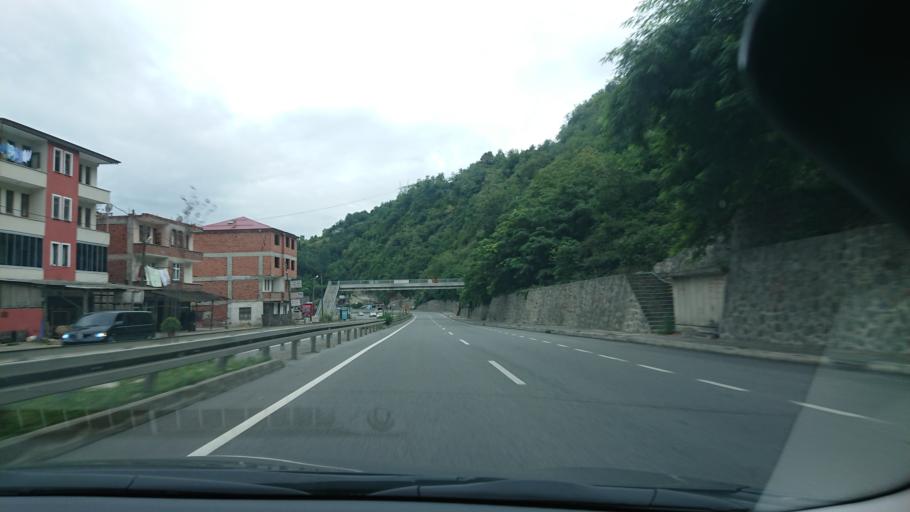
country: TR
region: Trabzon
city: Caglayan
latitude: 40.9482
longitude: 39.7408
